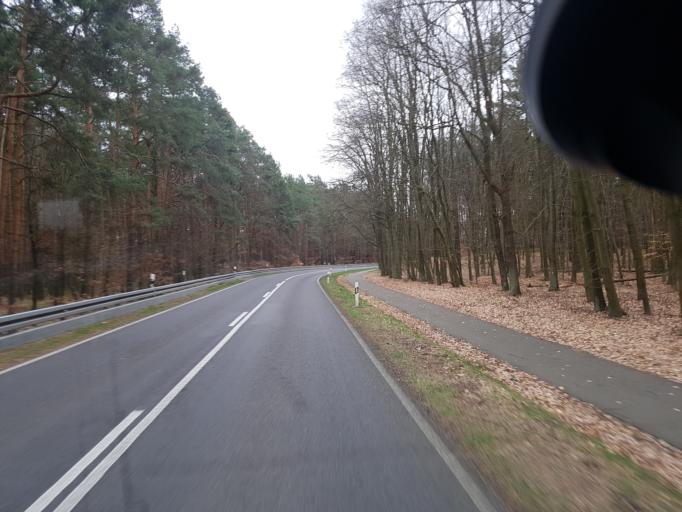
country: DE
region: Brandenburg
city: Mixdorf
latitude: 52.1864
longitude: 14.4719
